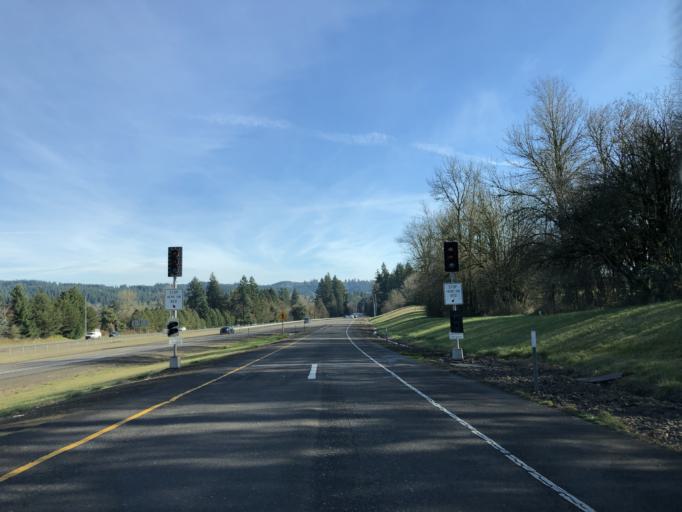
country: US
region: Oregon
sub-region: Clackamas County
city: Stafford
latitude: 45.3688
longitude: -122.7033
